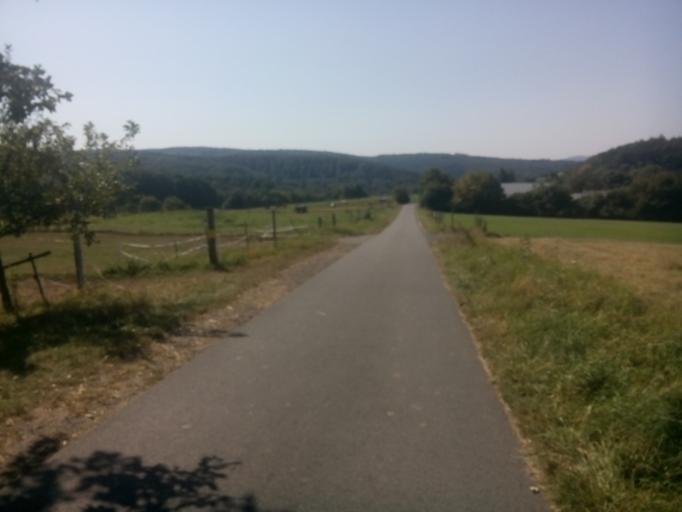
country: DE
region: Hesse
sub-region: Regierungsbezirk Darmstadt
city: Brensbach
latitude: 49.8162
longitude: 8.9137
